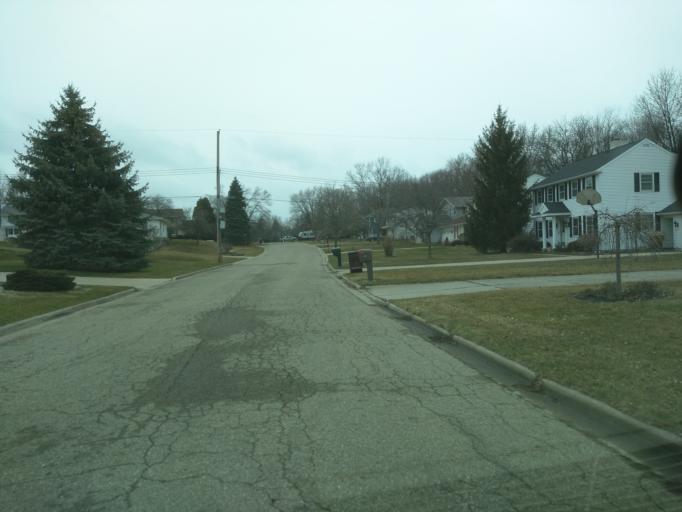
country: US
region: Michigan
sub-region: Eaton County
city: Waverly
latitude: 42.7589
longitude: -84.6252
